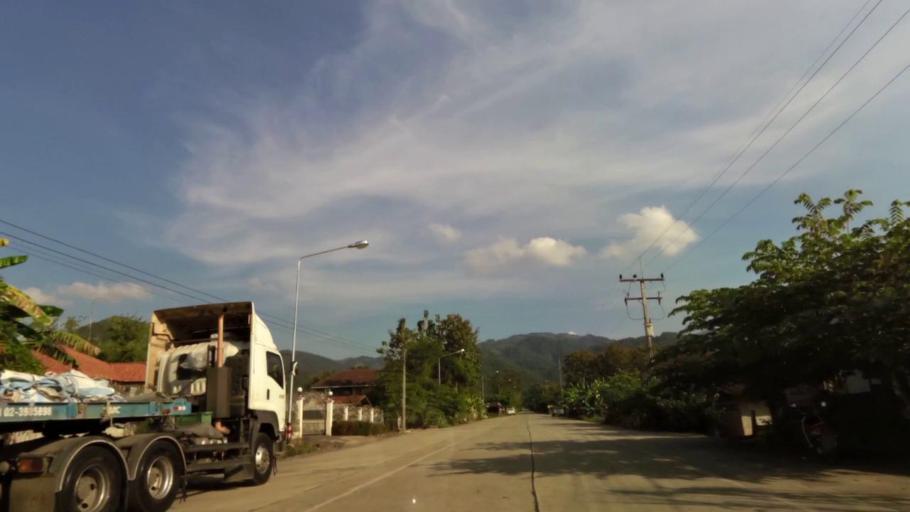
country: TH
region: Chiang Rai
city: Khun Tan
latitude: 19.8839
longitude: 100.2933
